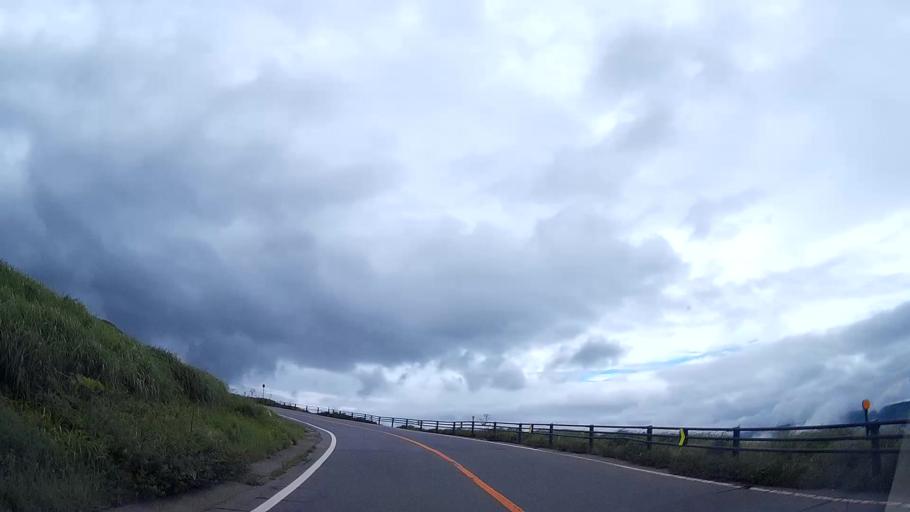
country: JP
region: Kumamoto
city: Aso
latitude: 32.9057
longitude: 131.0559
